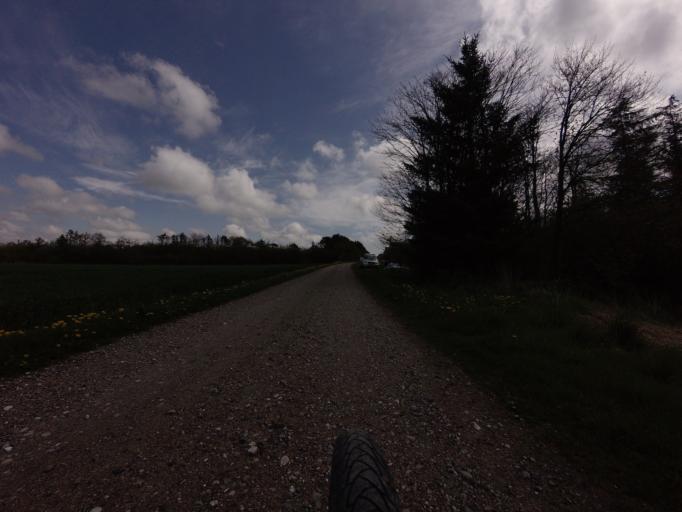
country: DK
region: North Denmark
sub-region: Jammerbugt Kommune
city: Kas
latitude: 57.1988
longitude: 9.6229
